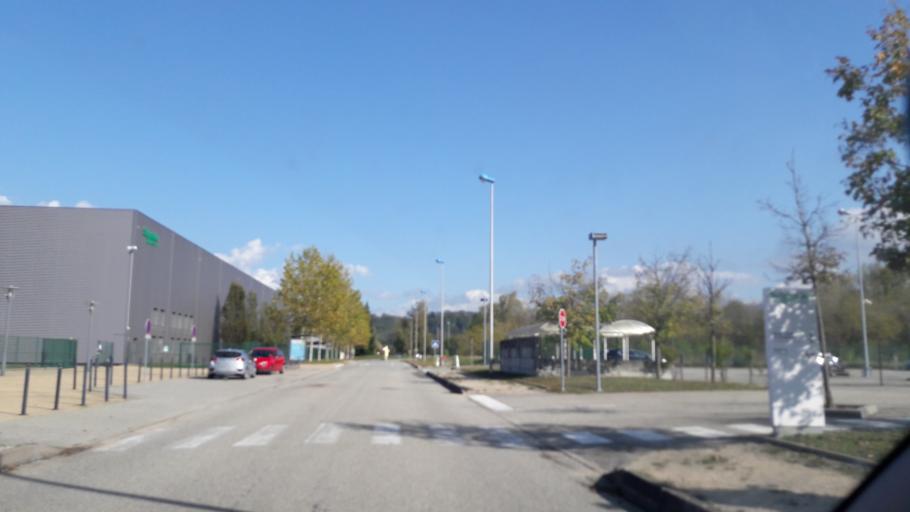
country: FR
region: Rhone-Alpes
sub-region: Departement de la Savoie
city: Montmelian
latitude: 45.4762
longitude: 6.0290
